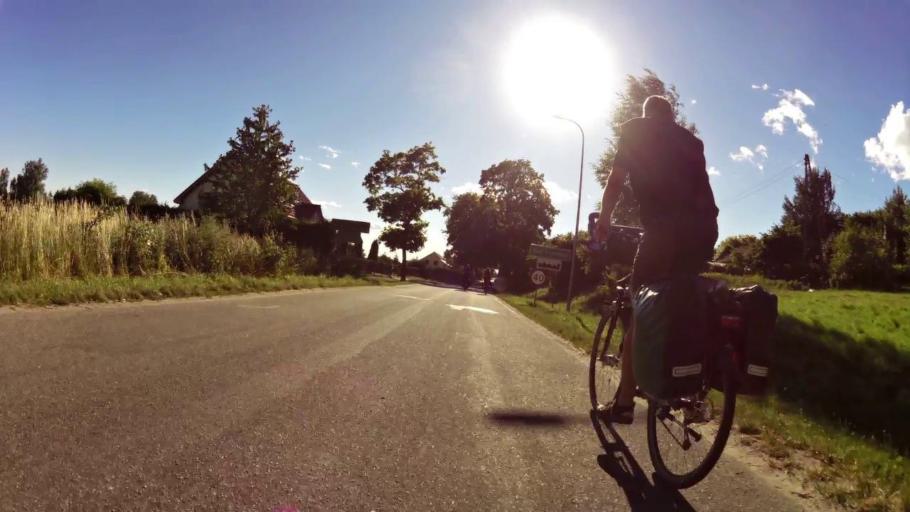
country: PL
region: West Pomeranian Voivodeship
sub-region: Powiat swidwinski
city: Swidwin
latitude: 53.7748
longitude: 15.7548
